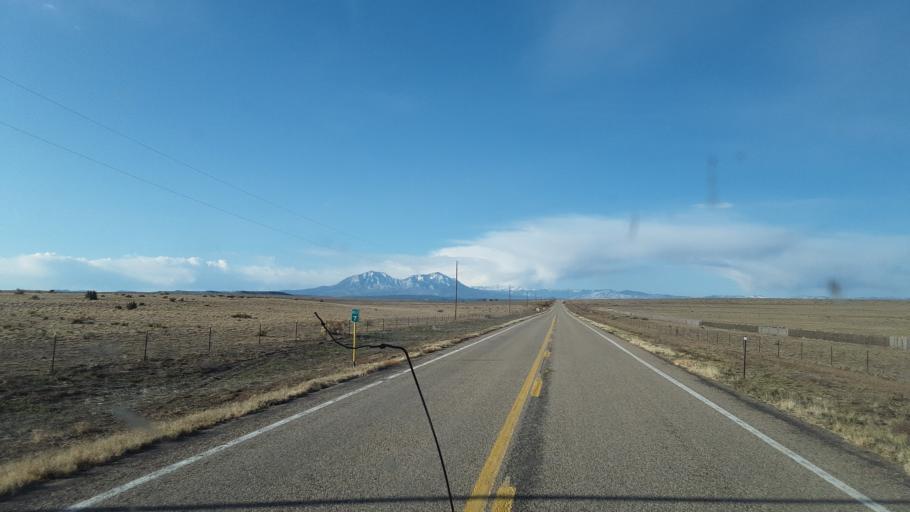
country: US
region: Colorado
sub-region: Huerfano County
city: Walsenburg
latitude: 37.6784
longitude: -104.6565
